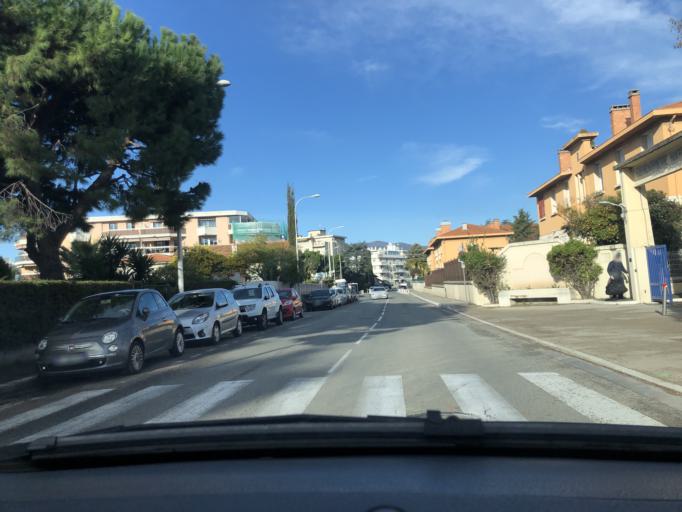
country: FR
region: Provence-Alpes-Cote d'Azur
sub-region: Departement des Alpes-Maritimes
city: Saint-Laurent-du-Var
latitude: 43.6805
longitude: 7.2084
